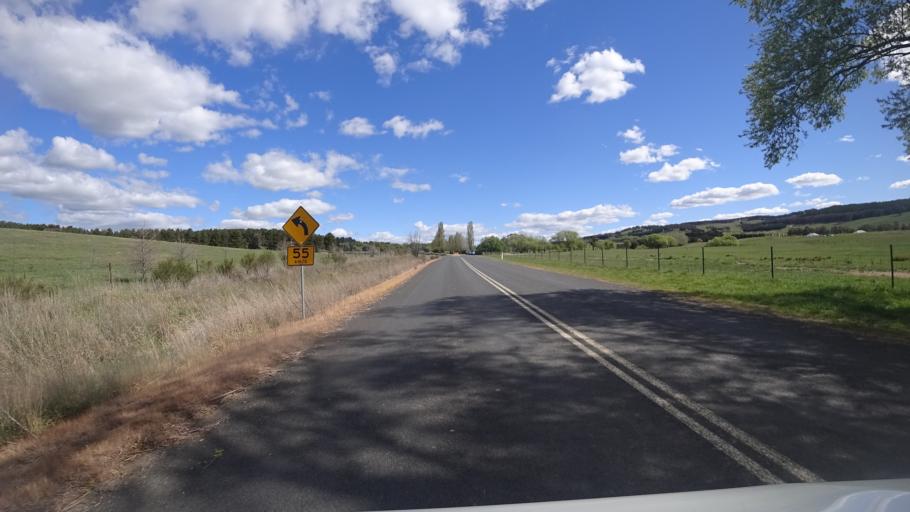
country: AU
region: New South Wales
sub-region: Oberon
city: Oberon
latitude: -33.6669
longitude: 149.7787
